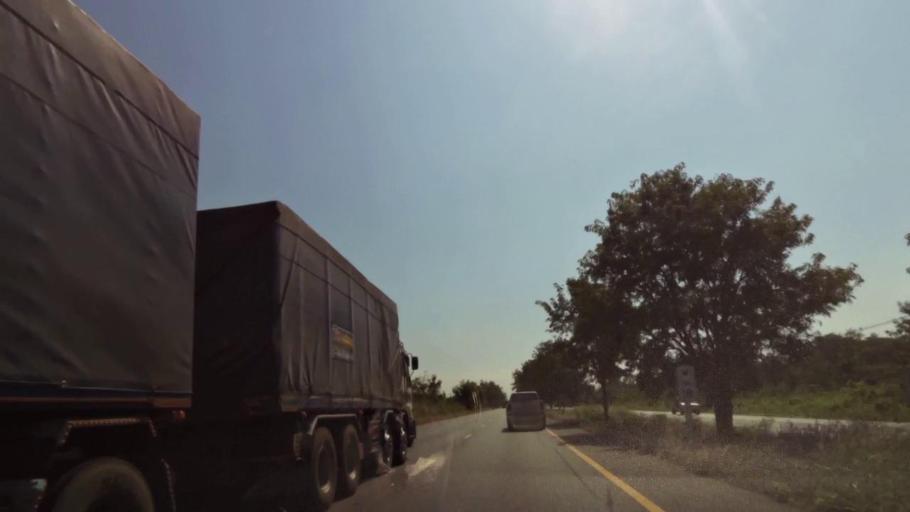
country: TH
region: Nakhon Sawan
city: Kao Liao
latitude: 15.8580
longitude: 100.1169
